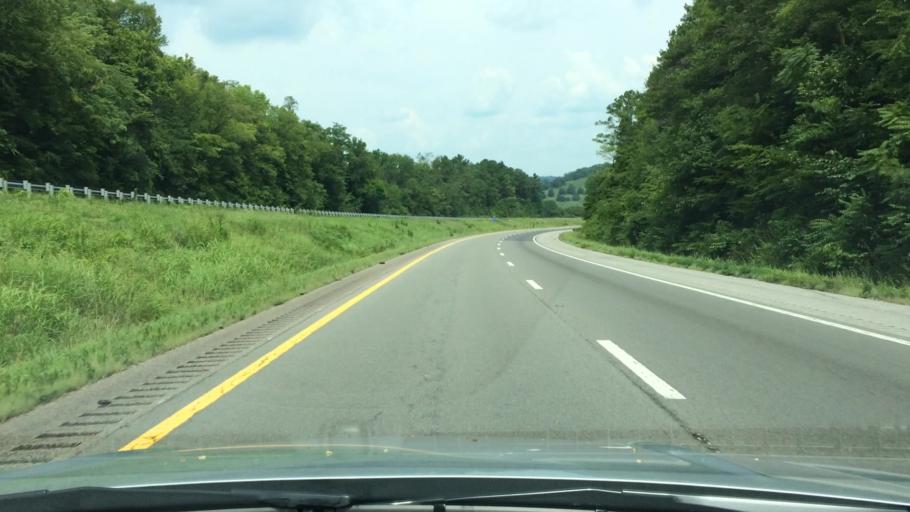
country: US
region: Tennessee
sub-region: Marshall County
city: Cornersville
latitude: 35.2665
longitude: -86.8883
